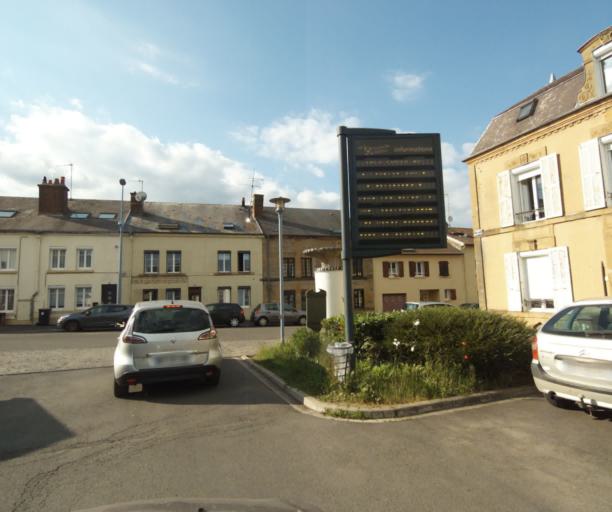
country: FR
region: Champagne-Ardenne
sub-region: Departement des Ardennes
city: Montcy-Notre-Dame
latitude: 49.7774
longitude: 4.7351
